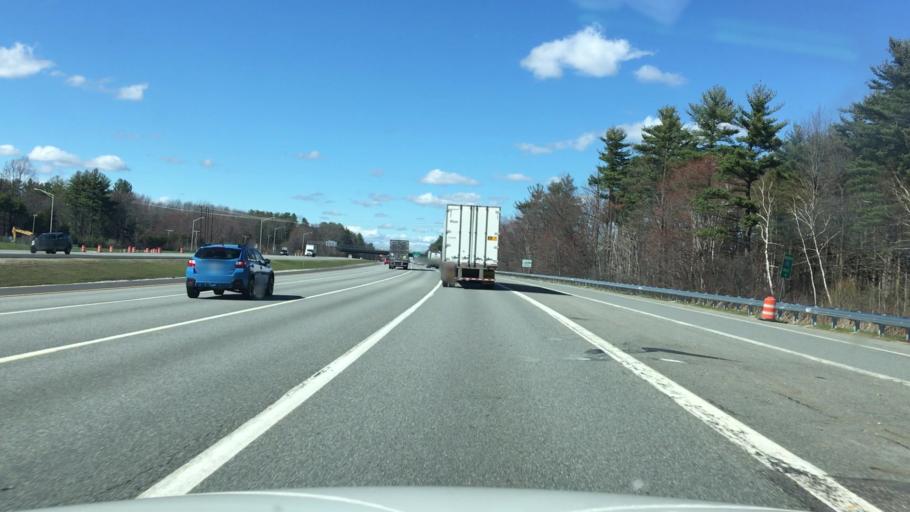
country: US
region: New Hampshire
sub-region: Rockingham County
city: Hampton Falls
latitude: 42.9364
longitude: -70.8614
